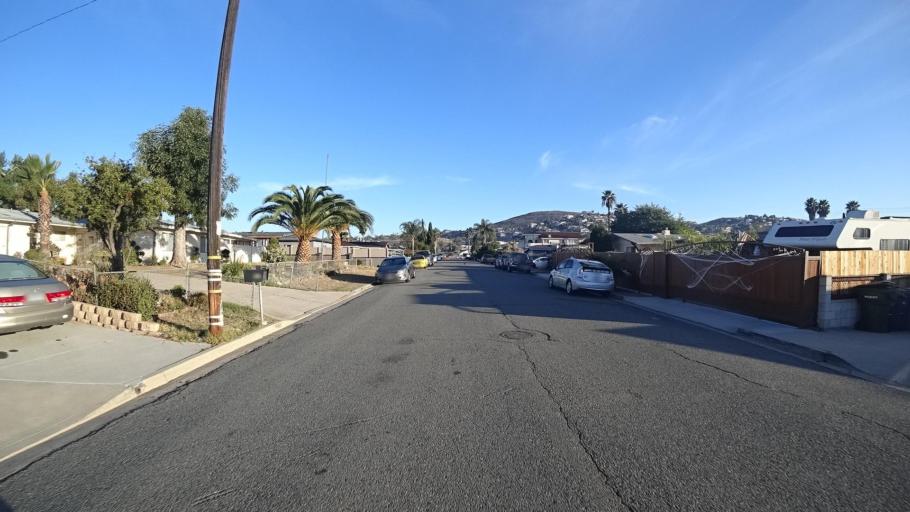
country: US
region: California
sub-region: San Diego County
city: La Presa
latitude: 32.7119
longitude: -116.9987
